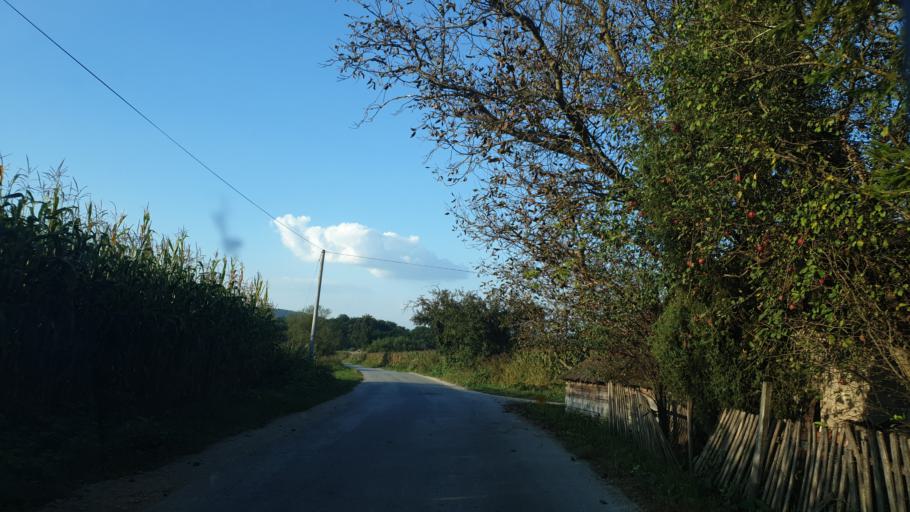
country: RS
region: Central Serbia
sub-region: Zlatiborski Okrug
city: Pozega
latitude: 43.8594
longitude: 19.9836
